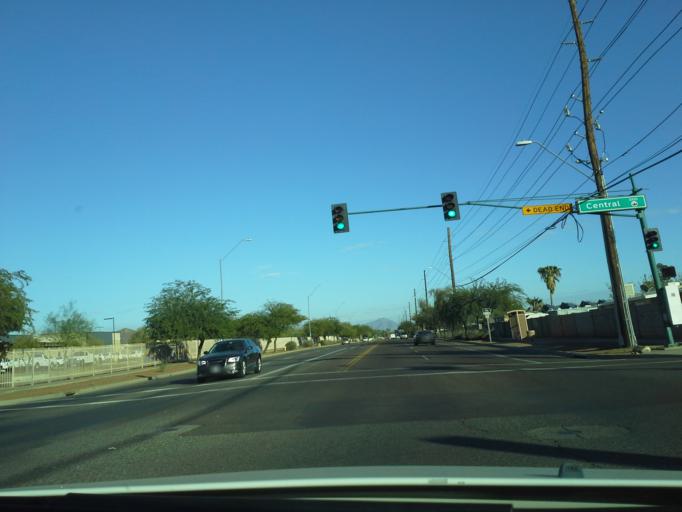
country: US
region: Arizona
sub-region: Maricopa County
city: Glendale
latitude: 33.6547
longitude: -112.0744
